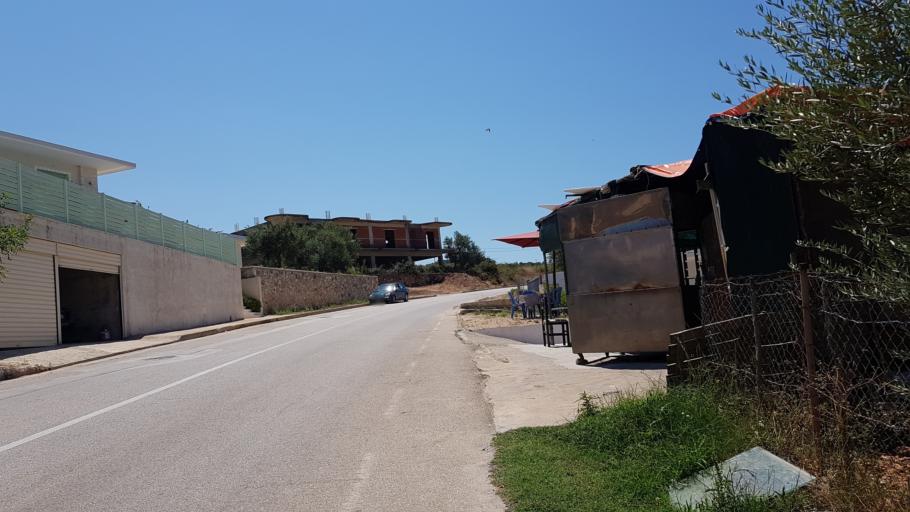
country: AL
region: Vlore
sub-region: Rrethi i Sarandes
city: Xarre
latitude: 39.7639
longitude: 20.0016
